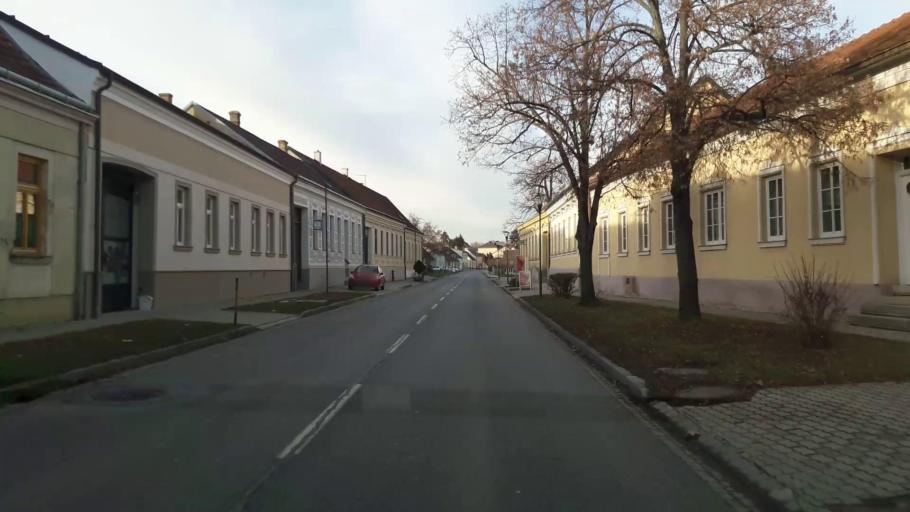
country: AT
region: Lower Austria
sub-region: Politischer Bezirk Ganserndorf
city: Bad Pirawarth
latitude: 48.4536
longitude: 16.5989
